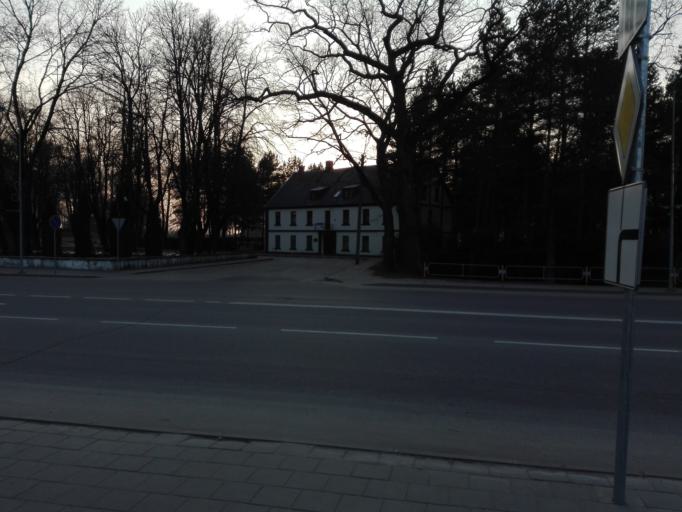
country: LT
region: Panevezys
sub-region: Birzai
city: Birzai
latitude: 56.2053
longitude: 24.7600
